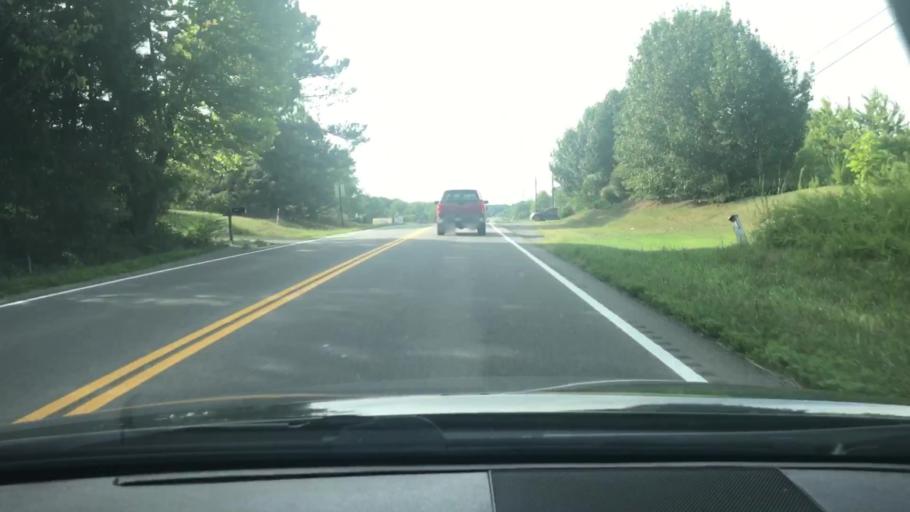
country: US
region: Tennessee
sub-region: Williamson County
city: Fairview
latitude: 36.0189
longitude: -87.1627
